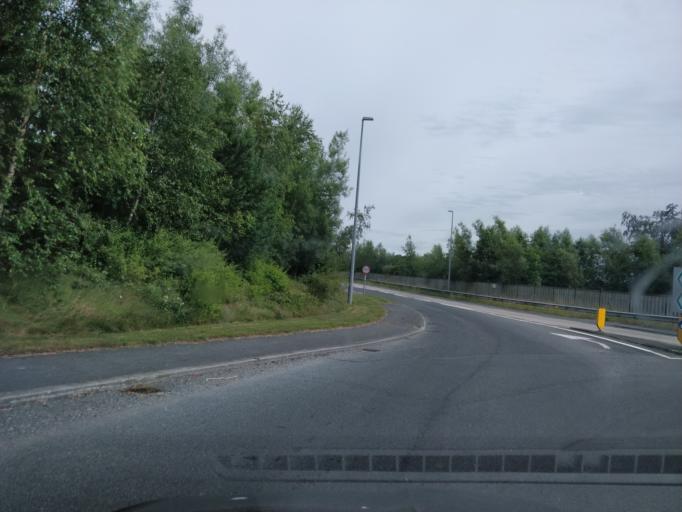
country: IE
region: Leinster
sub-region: Uibh Fhaili
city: Tullamore
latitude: 53.2517
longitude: -7.5151
